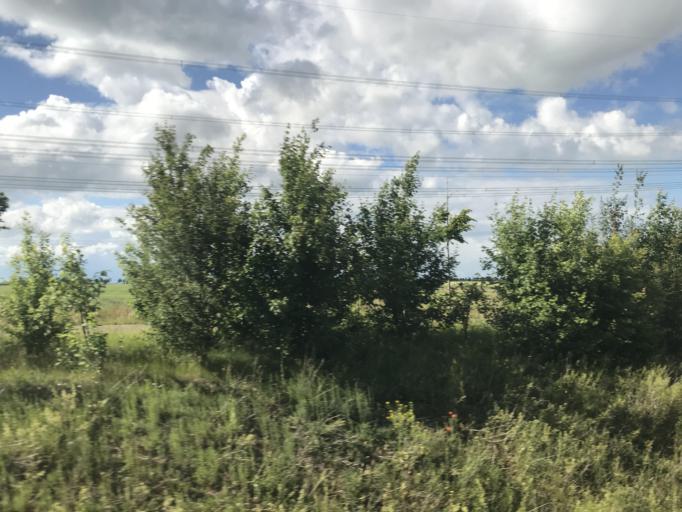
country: DE
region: Saxony-Anhalt
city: Langeneichstadt
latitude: 51.3195
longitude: 11.7239
